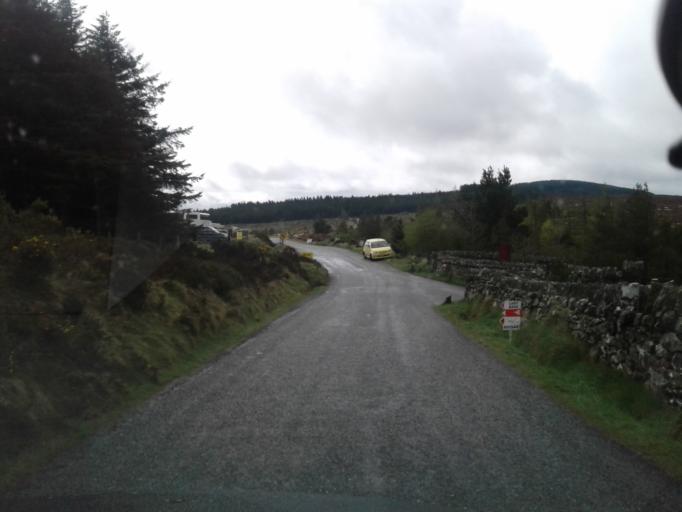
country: IE
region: Leinster
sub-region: Wicklow
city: Enniskerry
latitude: 53.0968
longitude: -6.2511
